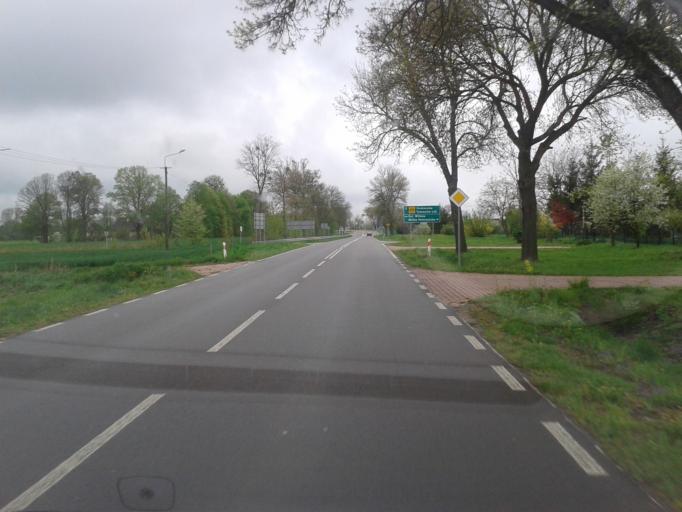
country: PL
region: Lublin Voivodeship
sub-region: Powiat hrubieszowski
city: Dolhobyczow
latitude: 50.5887
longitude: 23.9757
